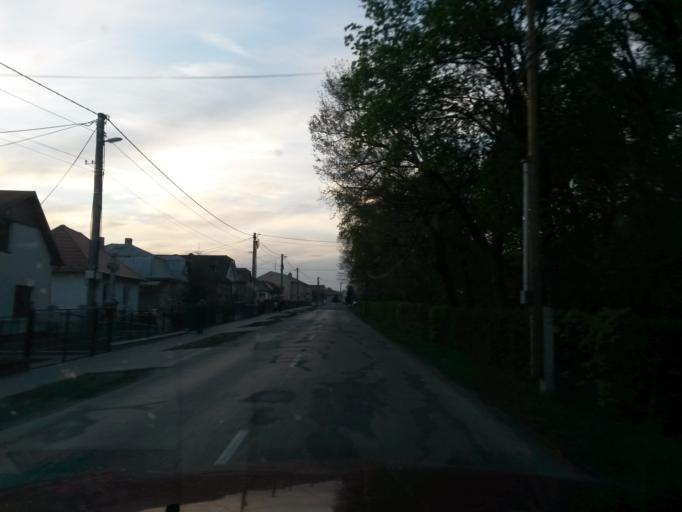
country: HU
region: Borsod-Abauj-Zemplen
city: Satoraljaujhely
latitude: 48.5242
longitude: 21.5866
